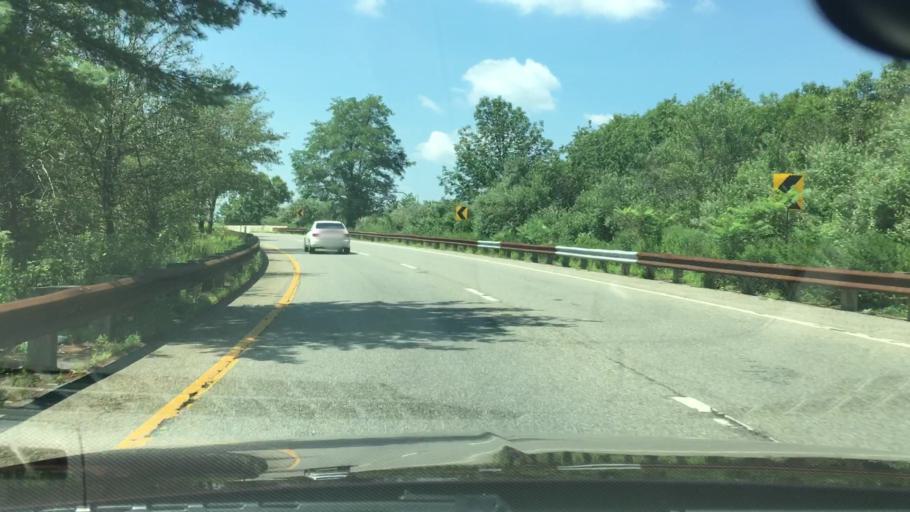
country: US
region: New York
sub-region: Suffolk County
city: Commack
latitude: 40.8071
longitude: -73.2806
